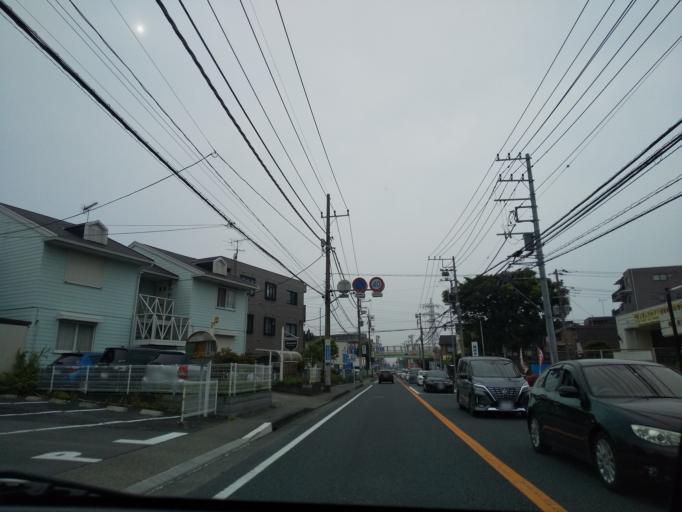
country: JP
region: Kanagawa
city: Zama
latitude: 35.5045
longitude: 139.4208
